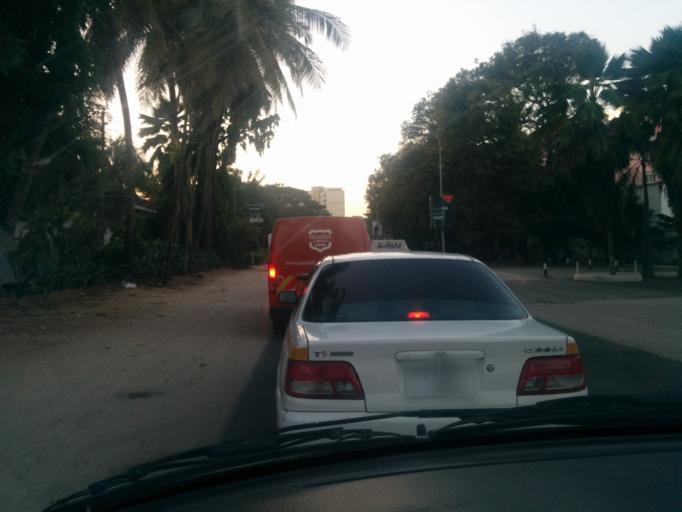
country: TZ
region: Dar es Salaam
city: Dar es Salaam
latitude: -6.8015
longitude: 39.2861
